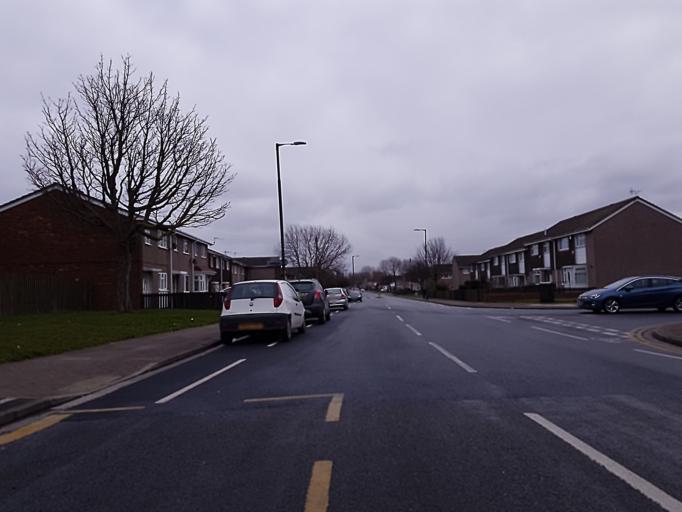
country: GB
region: England
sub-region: North East Lincolnshire
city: Great Coates
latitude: 53.5715
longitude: -0.1256
